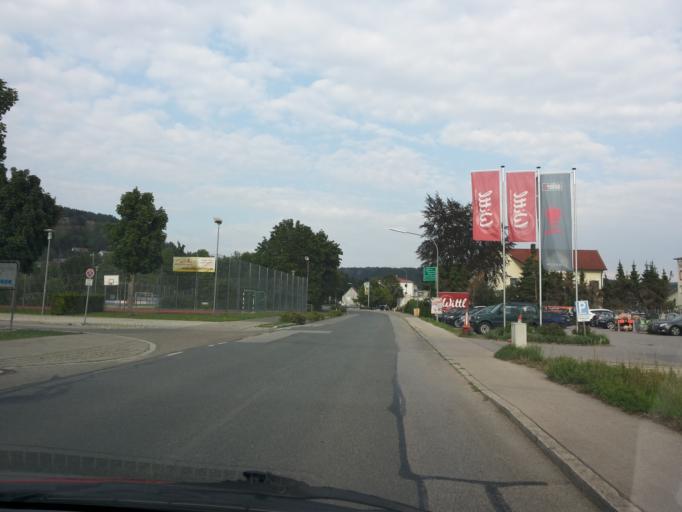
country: DE
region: Bavaria
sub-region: Upper Palatinate
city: Dietfurt
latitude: 49.0338
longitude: 11.5781
